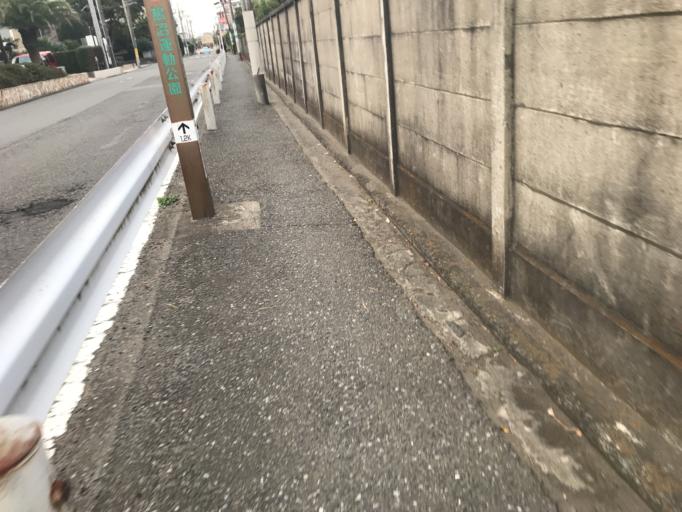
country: JP
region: Kanagawa
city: Fujisawa
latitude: 35.3179
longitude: 139.4694
